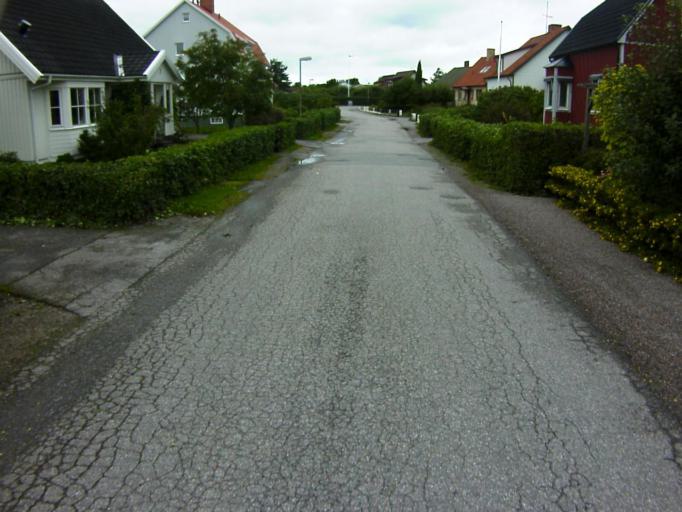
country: SE
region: Soedermanland
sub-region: Eskilstuna Kommun
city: Eskilstuna
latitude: 59.3769
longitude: 16.4835
